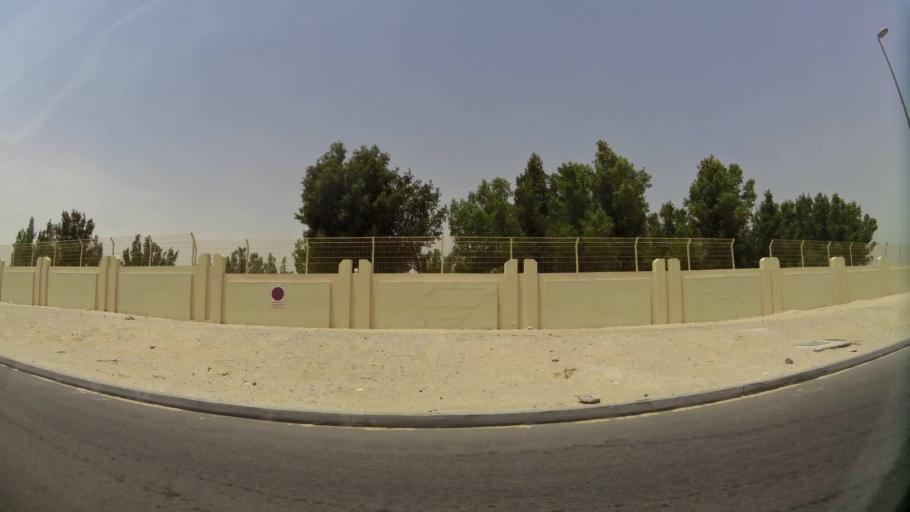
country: AE
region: Ash Shariqah
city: Sharjah
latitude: 25.2727
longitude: 55.4236
